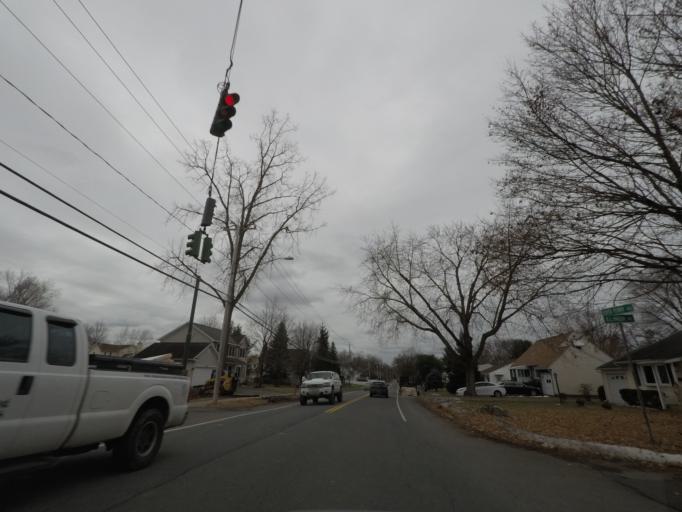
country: US
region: New York
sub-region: Schenectady County
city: Niskayuna
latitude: 42.7637
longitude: -73.7786
